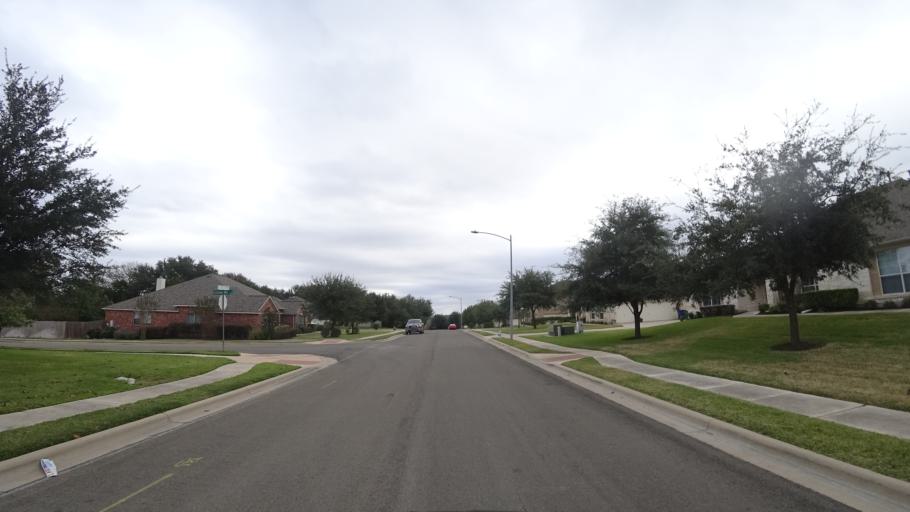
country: US
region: Texas
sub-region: Travis County
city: Shady Hollow
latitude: 30.1498
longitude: -97.8577
